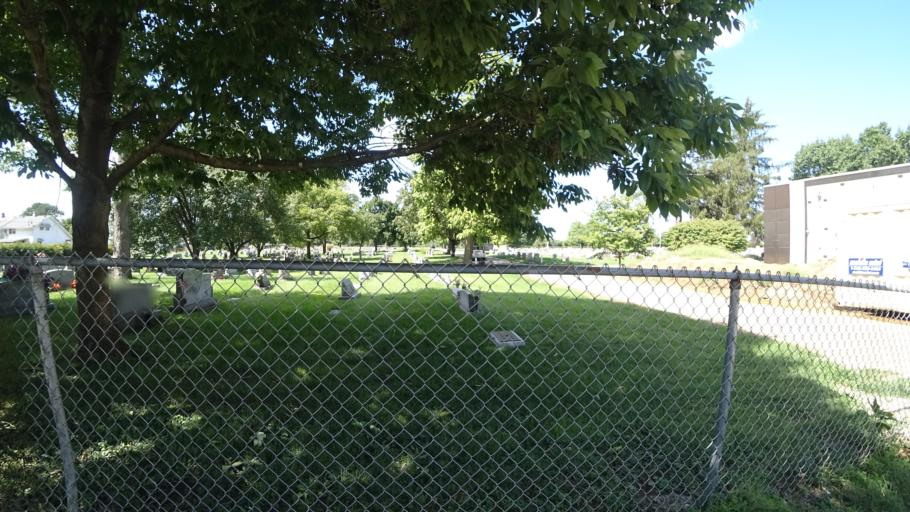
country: US
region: Ohio
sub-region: Butler County
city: Hamilton
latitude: 39.4062
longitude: -84.5435
